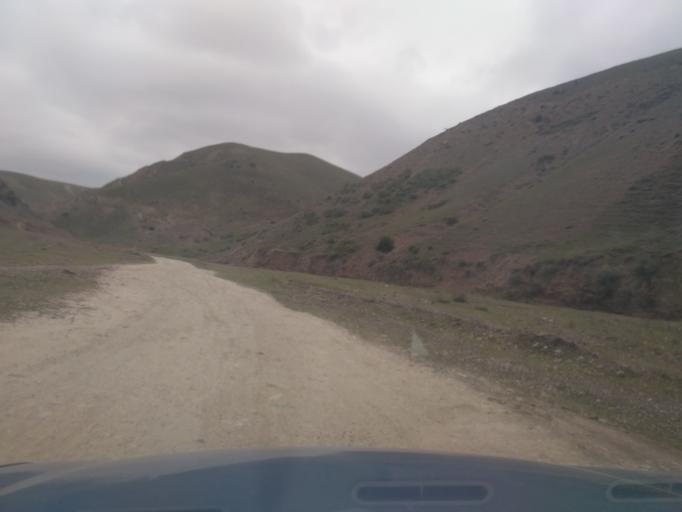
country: UZ
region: Jizzax
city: Zomin
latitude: 39.8485
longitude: 68.3968
